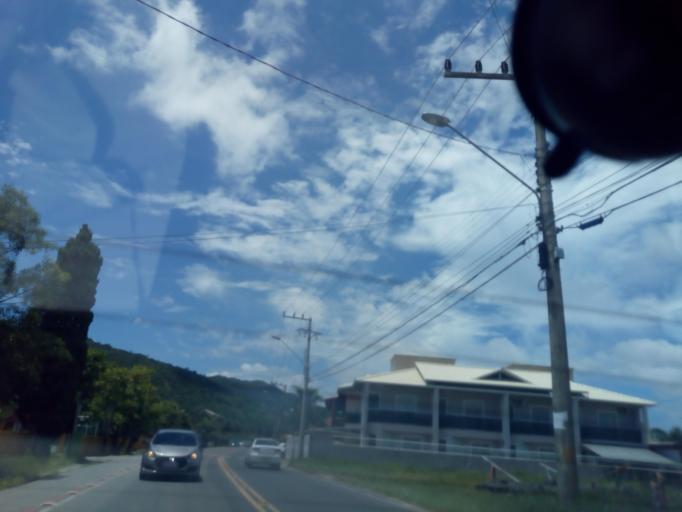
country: BR
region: Santa Catarina
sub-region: Florianopolis
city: Itacorubi
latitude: -27.3985
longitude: -48.4286
